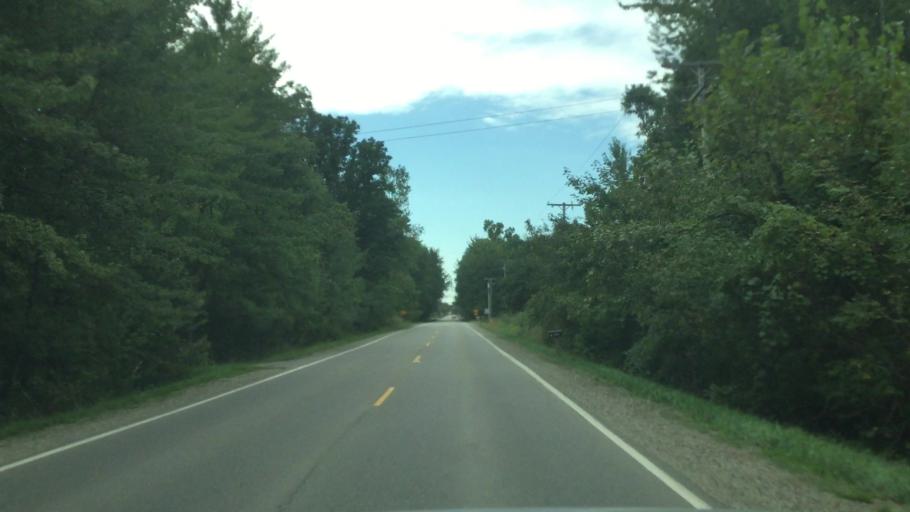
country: US
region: Michigan
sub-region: Genesee County
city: Argentine
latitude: 42.6788
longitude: -83.8381
